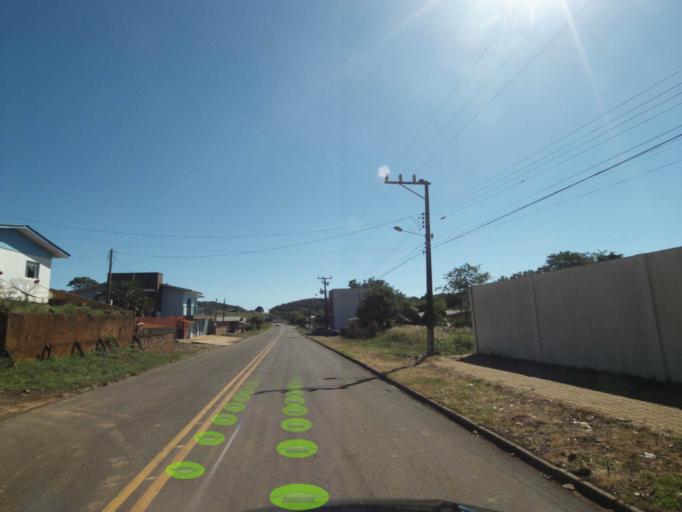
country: BR
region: Parana
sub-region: Coronel Vivida
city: Coronel Vivida
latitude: -26.1433
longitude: -52.3837
